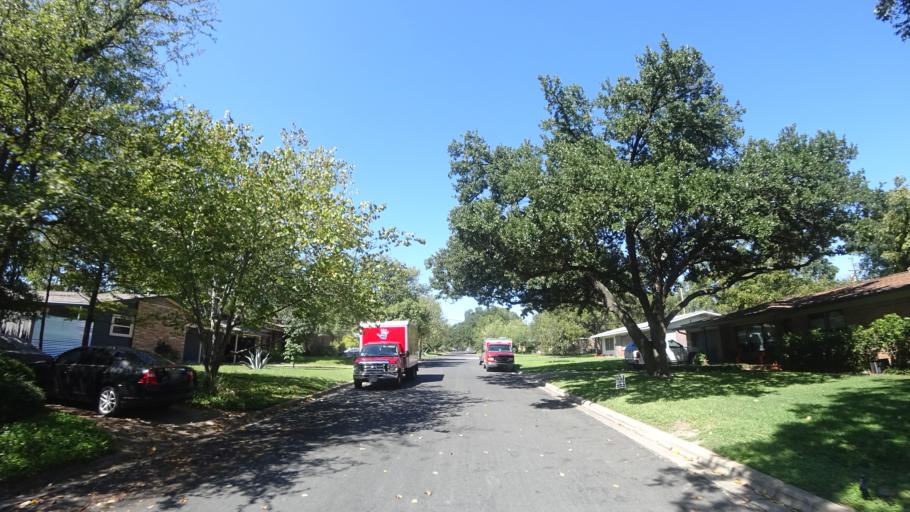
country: US
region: Texas
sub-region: Travis County
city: Austin
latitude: 30.3157
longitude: -97.6978
